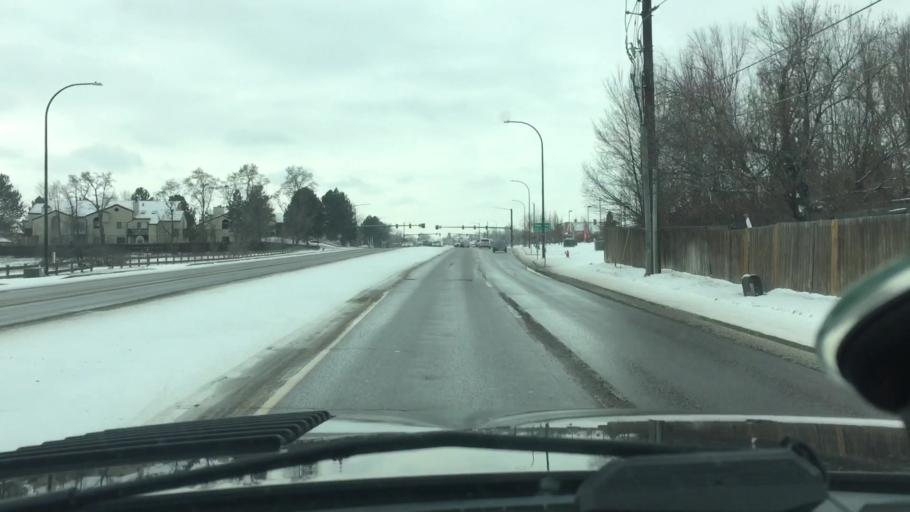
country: US
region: Colorado
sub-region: Adams County
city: Westminster
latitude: 39.8313
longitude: -105.0534
